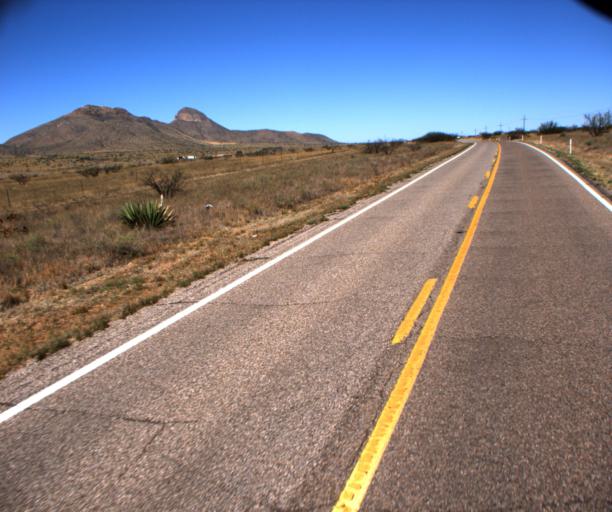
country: US
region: Arizona
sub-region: Cochise County
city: Huachuca City
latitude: 31.7083
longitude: -110.4447
